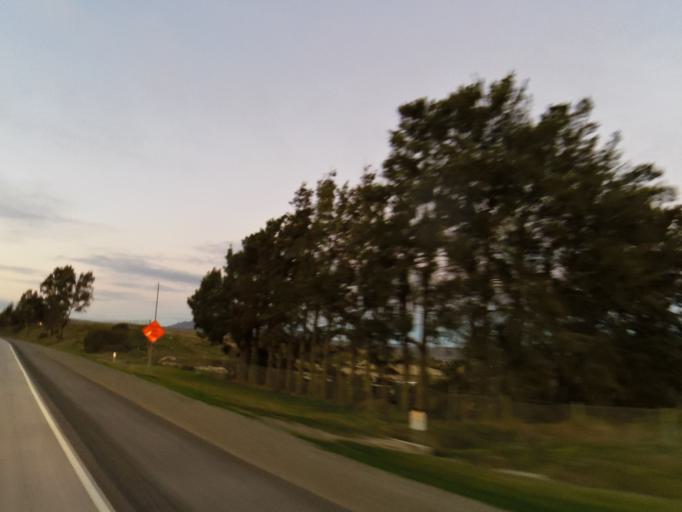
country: US
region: California
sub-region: Monterey County
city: Greenfield
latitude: 36.3181
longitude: -121.2350
